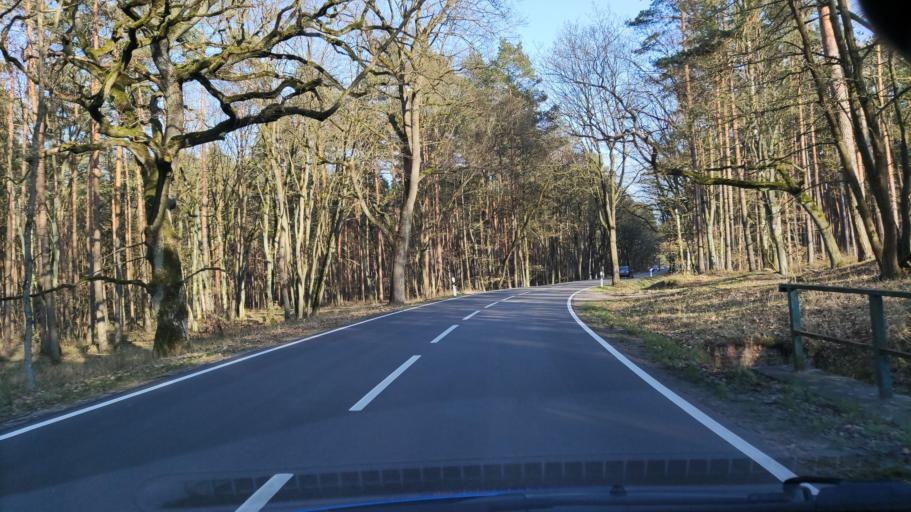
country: DE
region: Saxony-Anhalt
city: Seehausen
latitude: 52.8616
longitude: 11.7266
